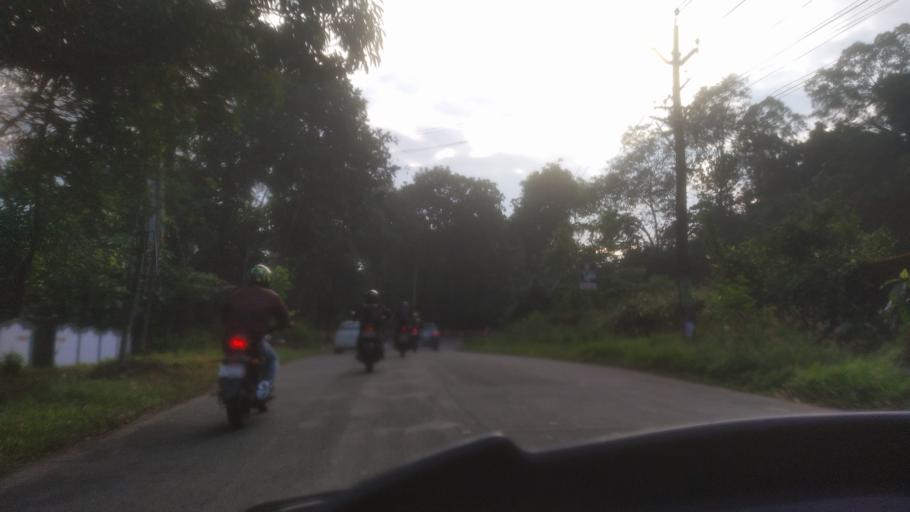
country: IN
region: Kerala
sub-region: Ernakulam
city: Perumpavur
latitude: 10.0973
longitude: 76.5499
